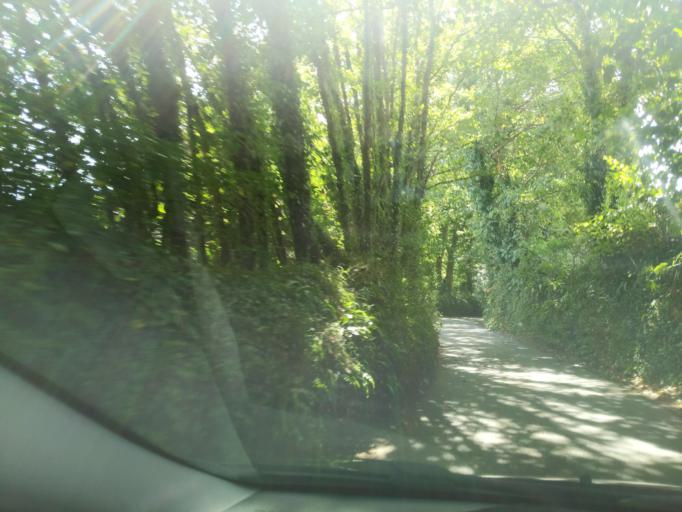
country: GB
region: England
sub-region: Cornwall
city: Torpoint
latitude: 50.3631
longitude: -4.2381
